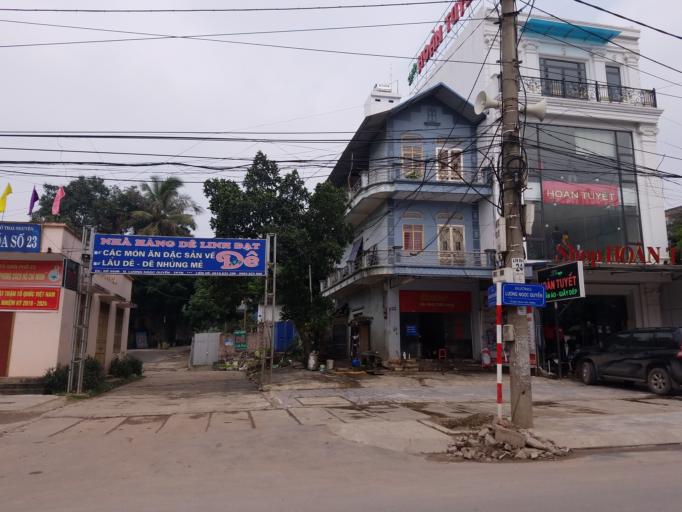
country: VN
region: Thai Nguyen
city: Thanh Pho Thai Nguyen
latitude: 21.5842
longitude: 105.8339
